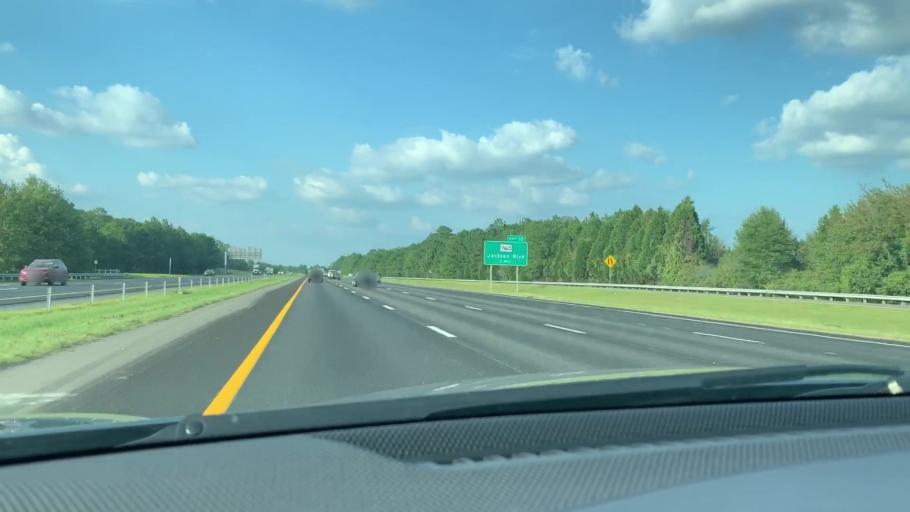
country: US
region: South Carolina
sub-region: Richland County
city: Forest Acres
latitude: 33.9787
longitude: -80.9543
